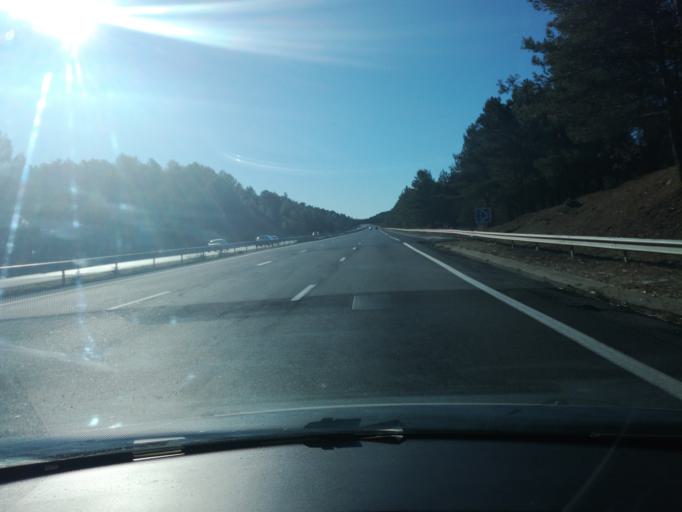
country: FR
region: Provence-Alpes-Cote d'Azur
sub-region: Departement des Bouches-du-Rhone
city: Fuveau
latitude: 43.4439
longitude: 5.5747
